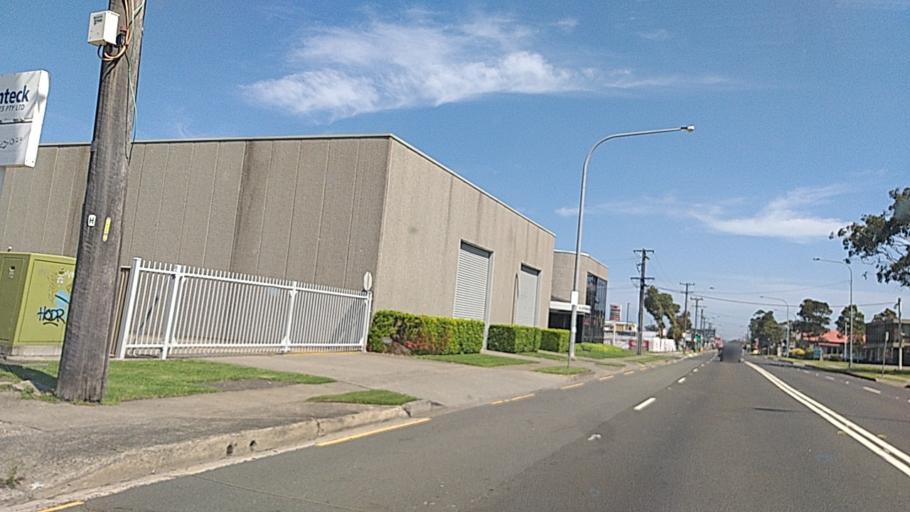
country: AU
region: New South Wales
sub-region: Wollongong
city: Fairy Meadow
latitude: -34.3863
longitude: 150.8944
